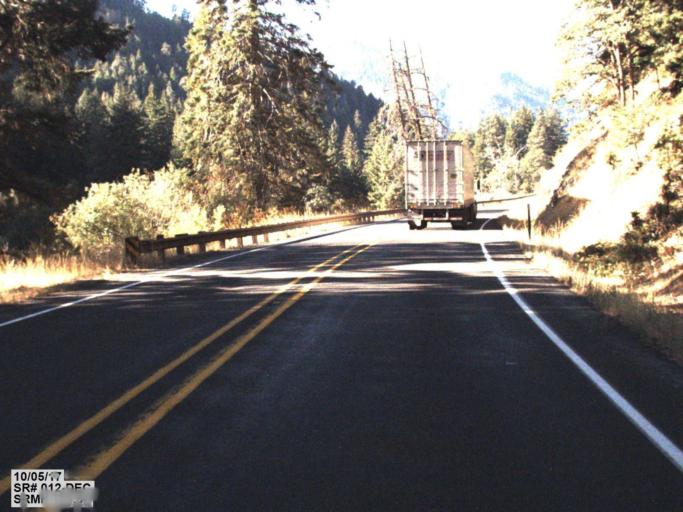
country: US
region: Washington
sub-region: Yakima County
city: Tieton
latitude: 46.6806
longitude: -120.9584
